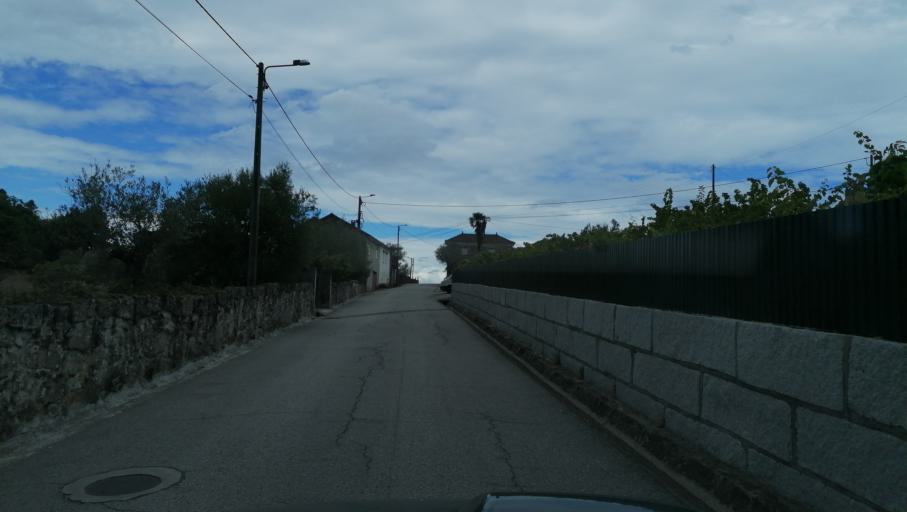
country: PT
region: Vila Real
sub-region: Vila Pouca de Aguiar
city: Vila Pouca de Aguiar
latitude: 41.5451
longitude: -7.6154
